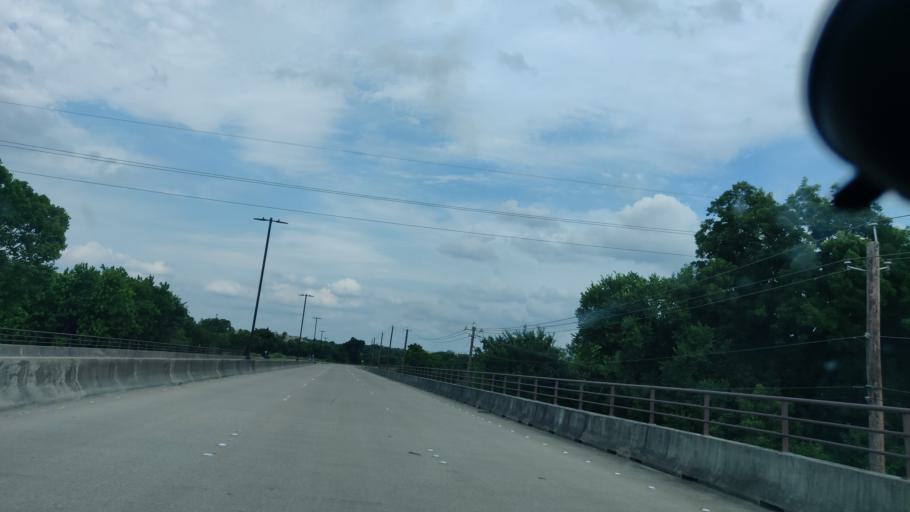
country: US
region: Texas
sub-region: Dallas County
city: Rowlett
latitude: 32.9313
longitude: -96.5933
